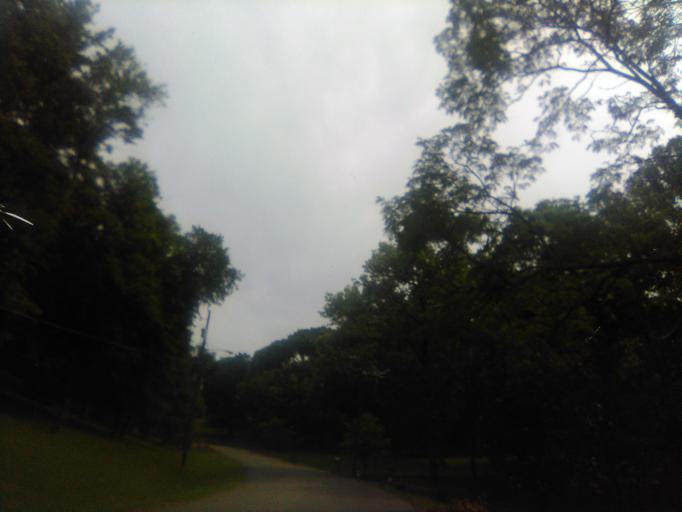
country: US
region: Tennessee
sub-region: Davidson County
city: Belle Meade
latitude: 36.0932
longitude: -86.8944
